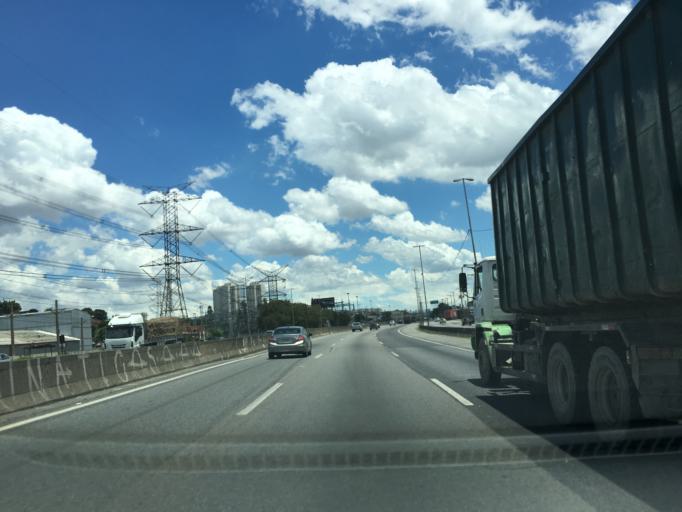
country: BR
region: Sao Paulo
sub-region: Guarulhos
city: Guarulhos
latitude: -23.4769
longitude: -46.5604
